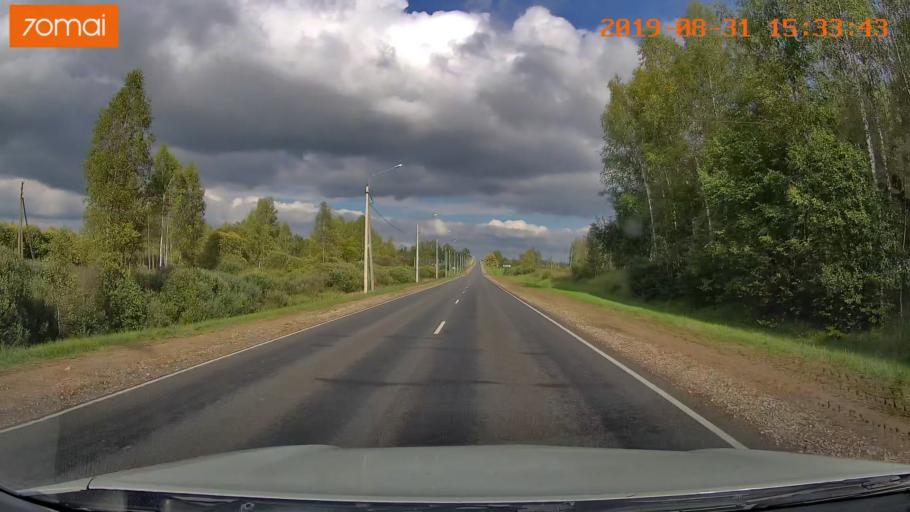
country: RU
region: Kaluga
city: Mosal'sk
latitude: 54.5968
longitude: 34.7065
